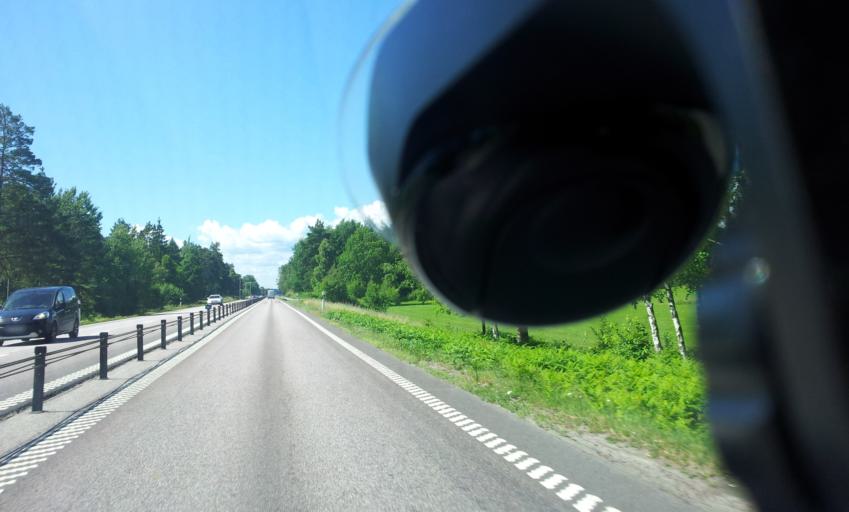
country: SE
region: Kalmar
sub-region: Monsteras Kommun
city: Moensteras
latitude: 57.0751
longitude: 16.4784
